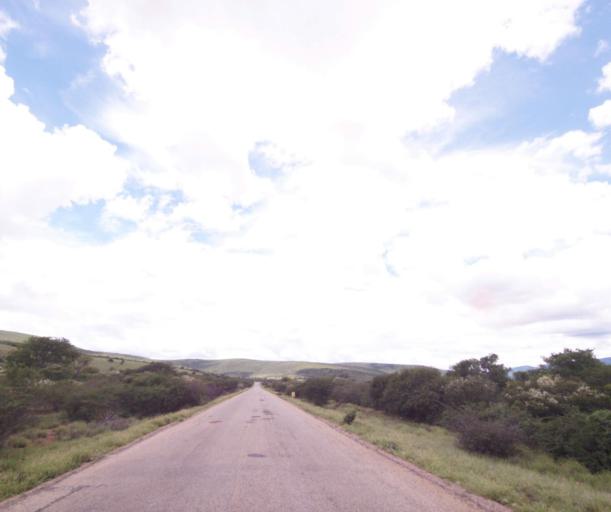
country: BR
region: Bahia
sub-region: Brumado
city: Brumado
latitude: -14.1884
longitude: -41.5757
